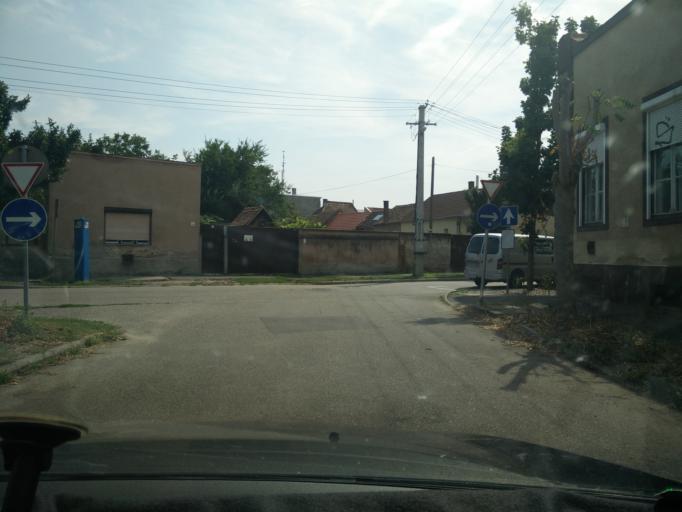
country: HU
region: Hajdu-Bihar
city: Debrecen
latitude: 47.5324
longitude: 21.6175
